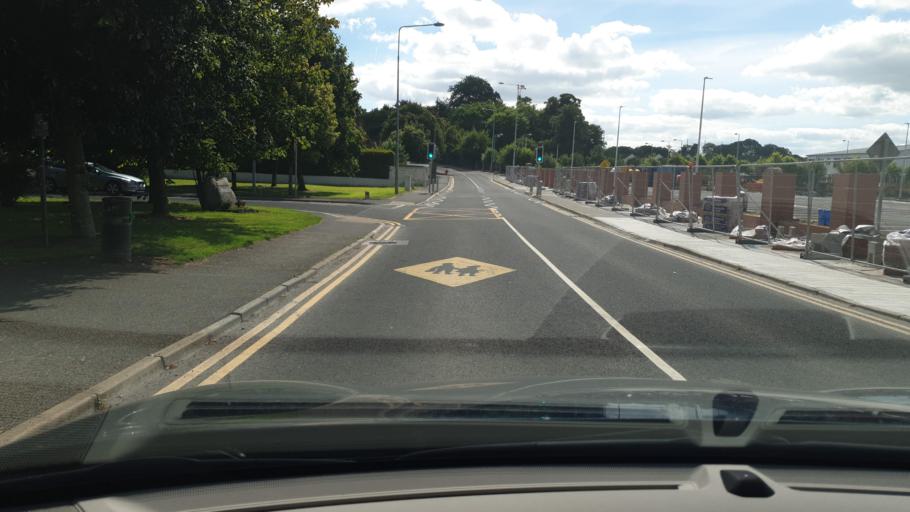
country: IE
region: Leinster
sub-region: An Mhi
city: Dunboyne
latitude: 53.4161
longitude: -6.4717
